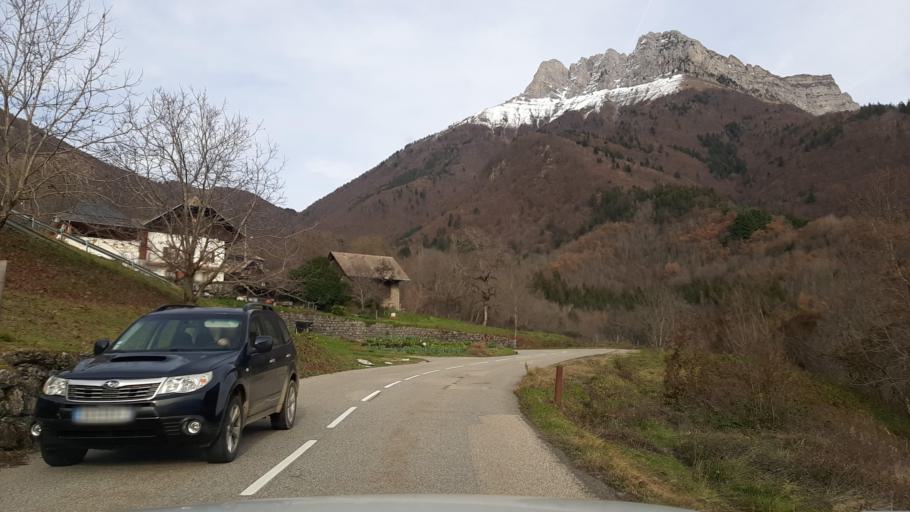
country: FR
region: Rhone-Alpes
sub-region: Departement de la Savoie
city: Coise-Saint-Jean-Pied-Gauthier
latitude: 45.5777
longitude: 6.1531
